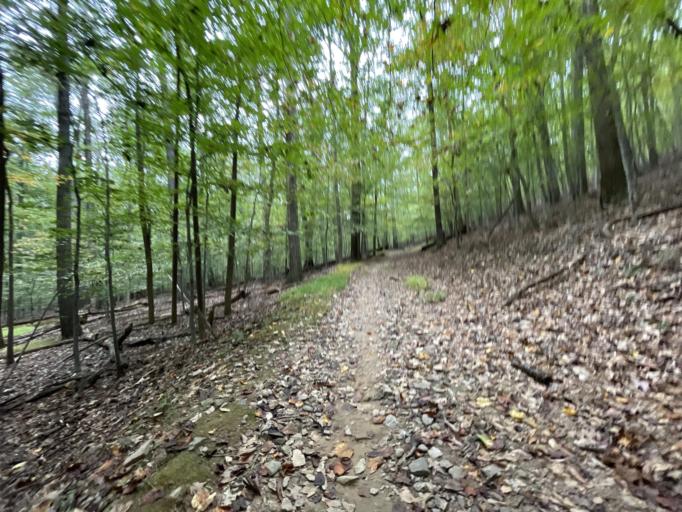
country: US
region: Maryland
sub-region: Baltimore County
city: Hampton
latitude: 39.4295
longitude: -76.5710
